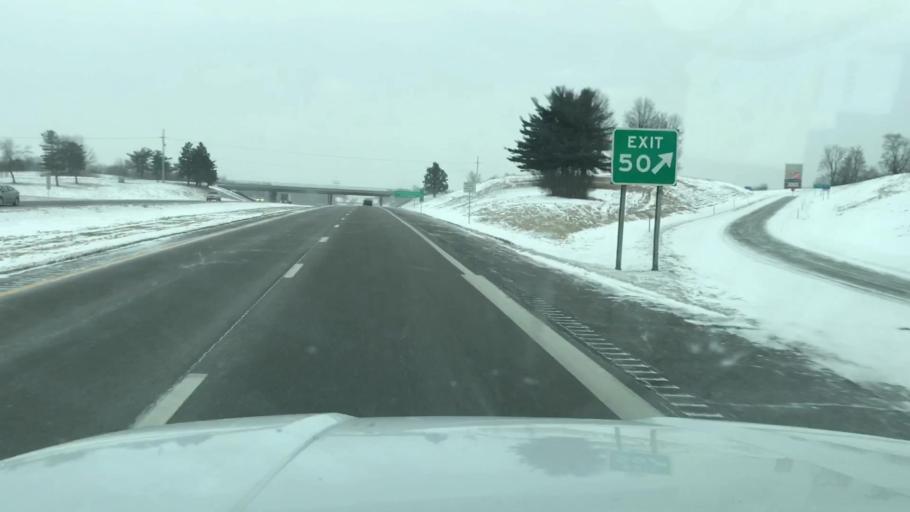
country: US
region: Missouri
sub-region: Andrew County
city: Country Club Village
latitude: 39.8178
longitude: -94.8048
